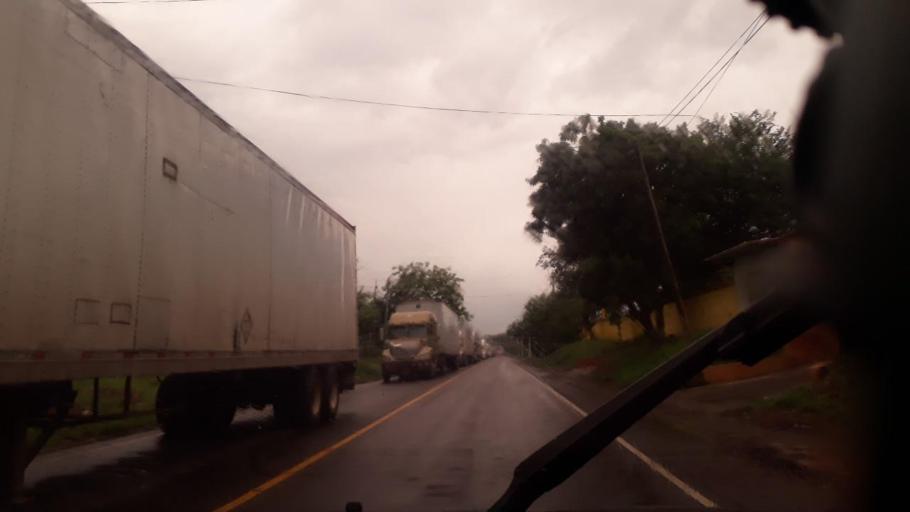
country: SV
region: Ahuachapan
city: San Francisco Menendez
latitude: 13.8802
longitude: -90.1069
